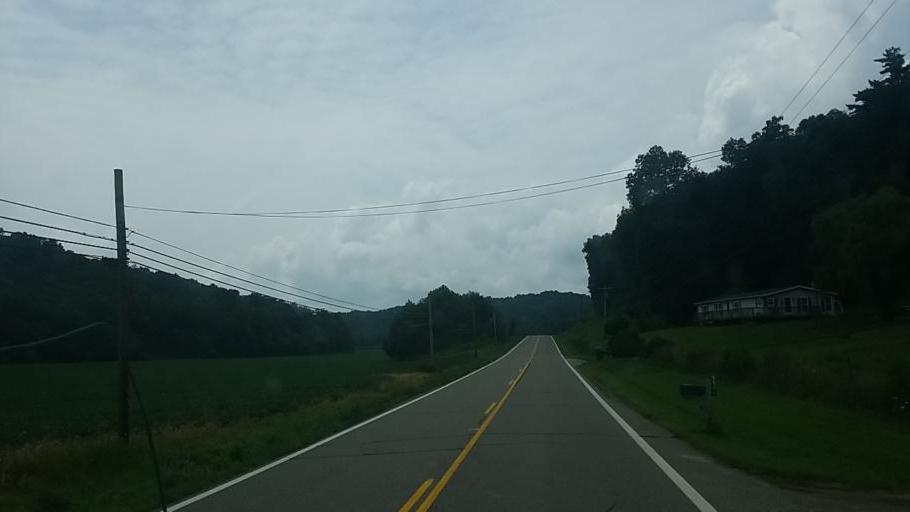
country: US
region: Ohio
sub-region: Licking County
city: Newark
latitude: 40.1627
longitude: -82.2849
